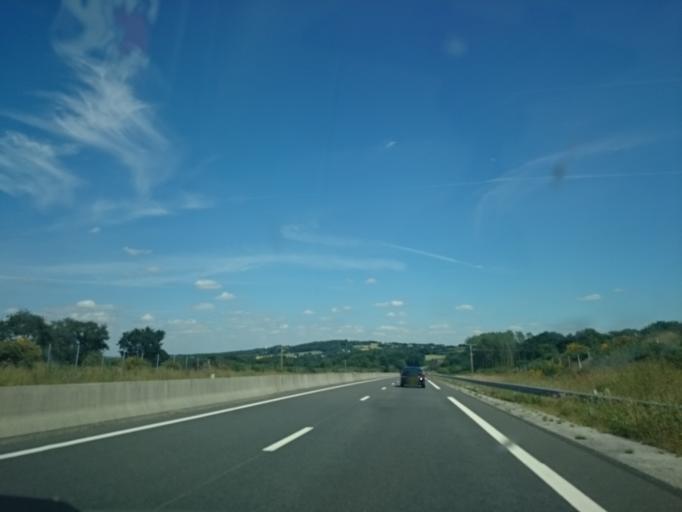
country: FR
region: Brittany
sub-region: Departement des Cotes-d'Armor
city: Gouarec
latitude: 48.2302
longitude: -3.1248
